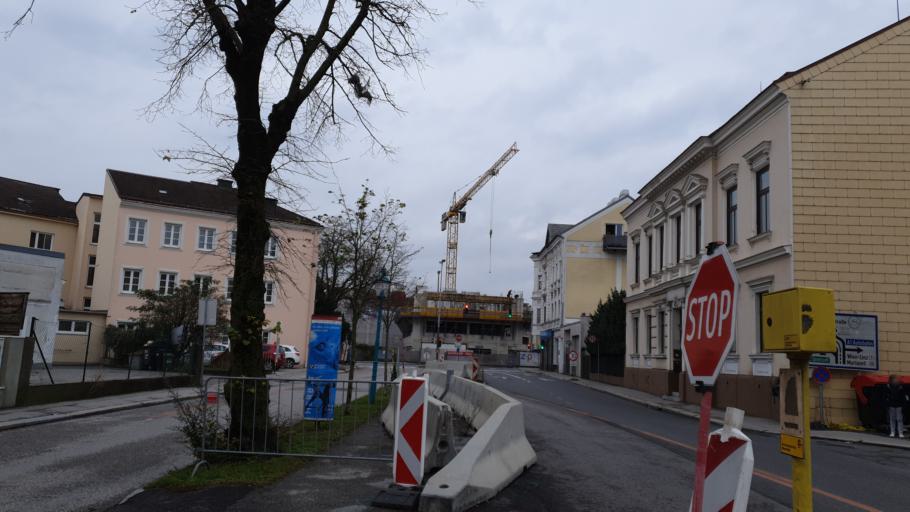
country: AT
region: Lower Austria
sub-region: Sankt Polten Stadt
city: Sankt Poelten
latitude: 48.2026
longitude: 15.6211
